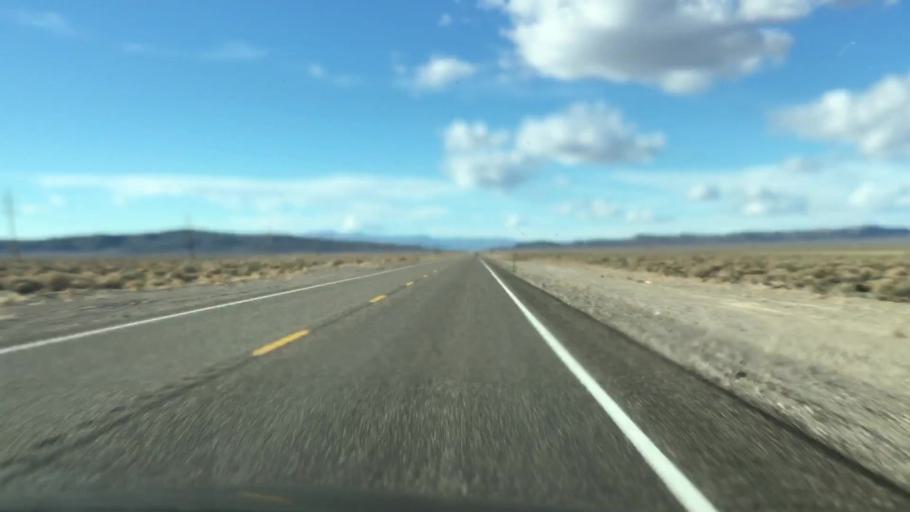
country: US
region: Nevada
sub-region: Nye County
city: Beatty
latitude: 37.1343
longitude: -116.8481
